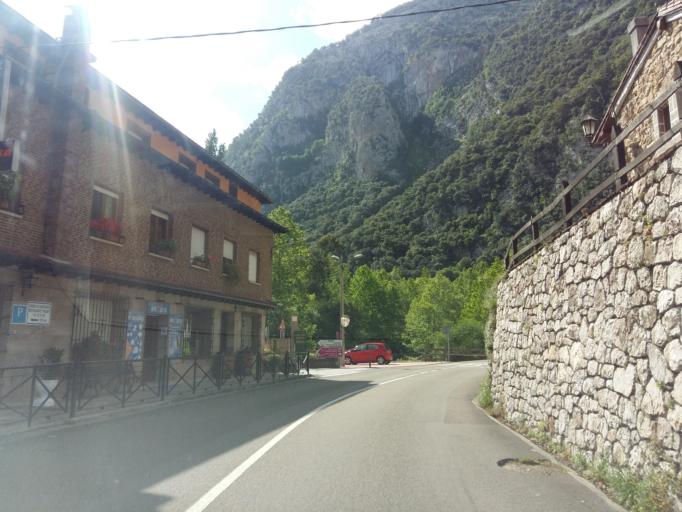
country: ES
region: Cantabria
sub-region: Provincia de Cantabria
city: Tresviso
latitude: 43.2542
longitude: -4.6134
